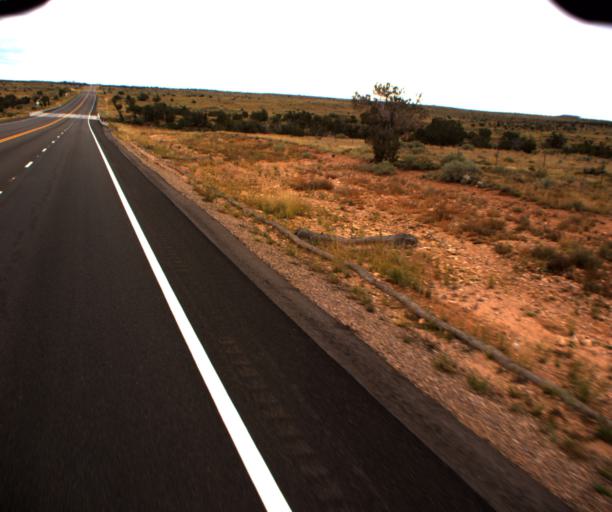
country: US
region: Arizona
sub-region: Navajo County
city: Snowflake
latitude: 34.5938
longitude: -110.0870
